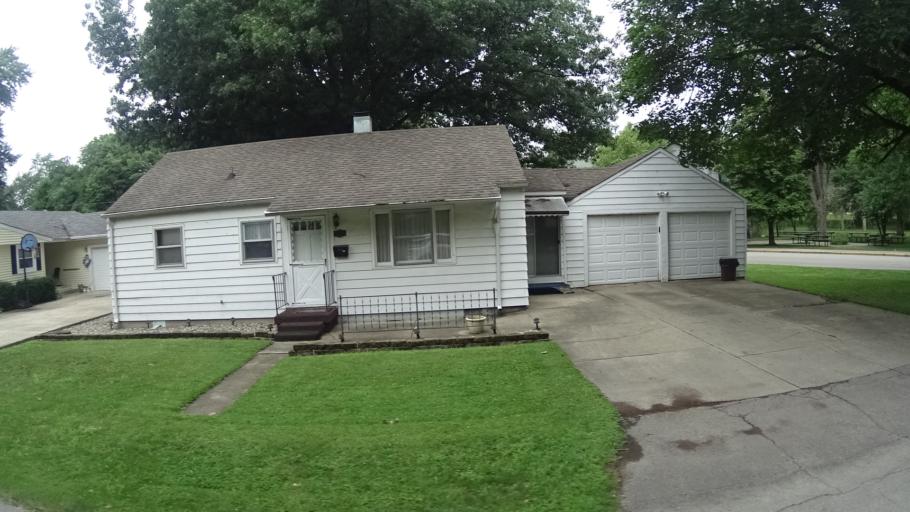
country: US
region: Indiana
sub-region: Madison County
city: Pendleton
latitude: 40.0058
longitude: -85.7425
